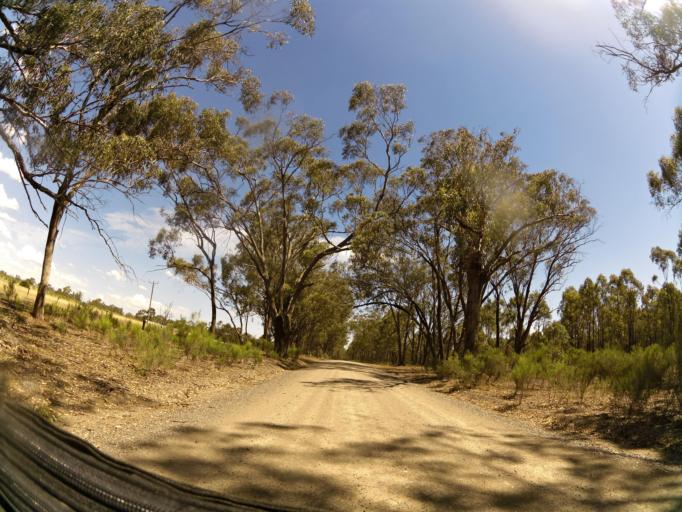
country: AU
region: Victoria
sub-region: Campaspe
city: Kyabram
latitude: -36.8186
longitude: 145.0803
